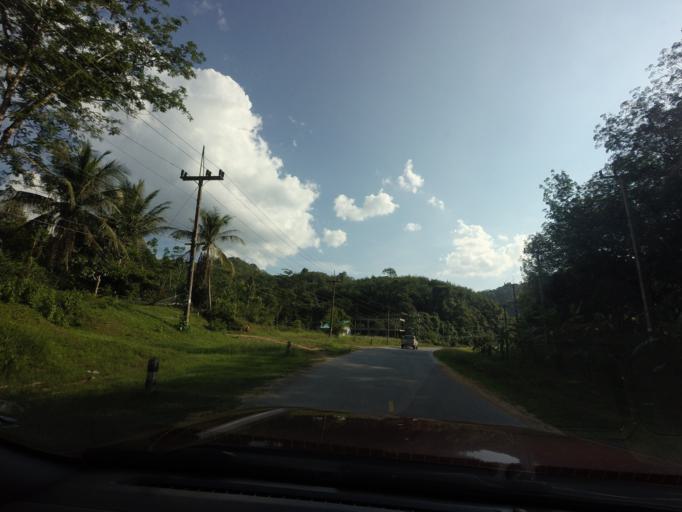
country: TH
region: Yala
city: Ban Nang Sata
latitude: 6.1955
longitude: 101.2540
